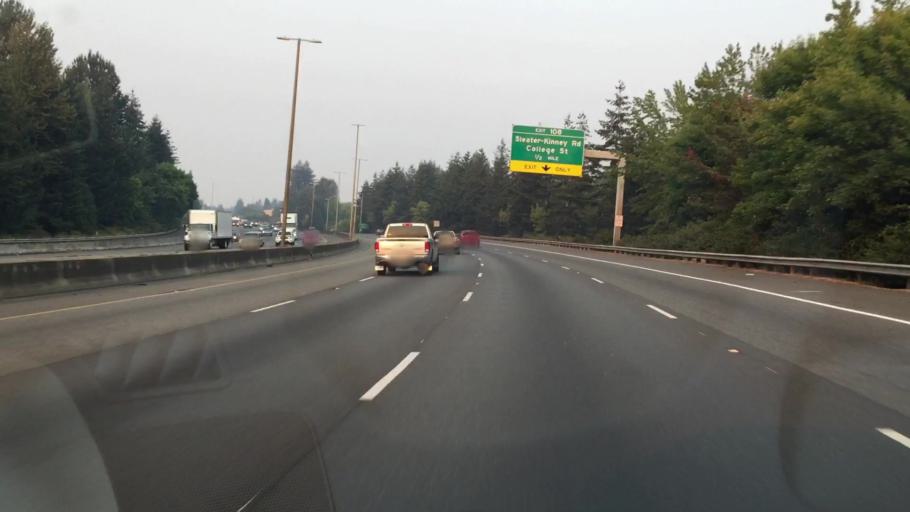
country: US
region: Washington
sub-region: Thurston County
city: Lacey
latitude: 47.0403
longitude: -122.8554
